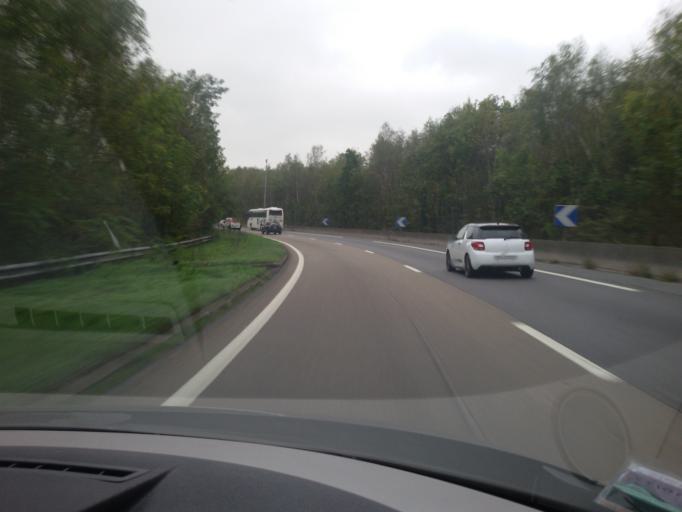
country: FR
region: Ile-de-France
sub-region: Departement de l'Essonne
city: Les Ulis
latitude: 48.6567
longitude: 2.1780
